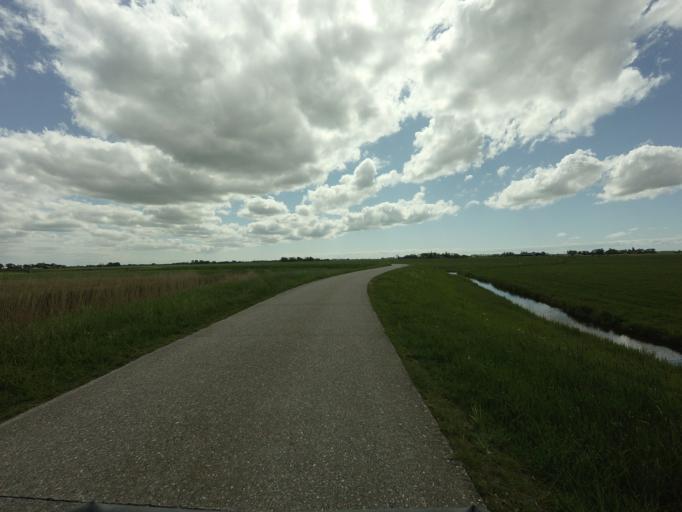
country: NL
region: Friesland
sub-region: Gemeente Littenseradiel
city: Wommels
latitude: 53.1160
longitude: 5.5507
